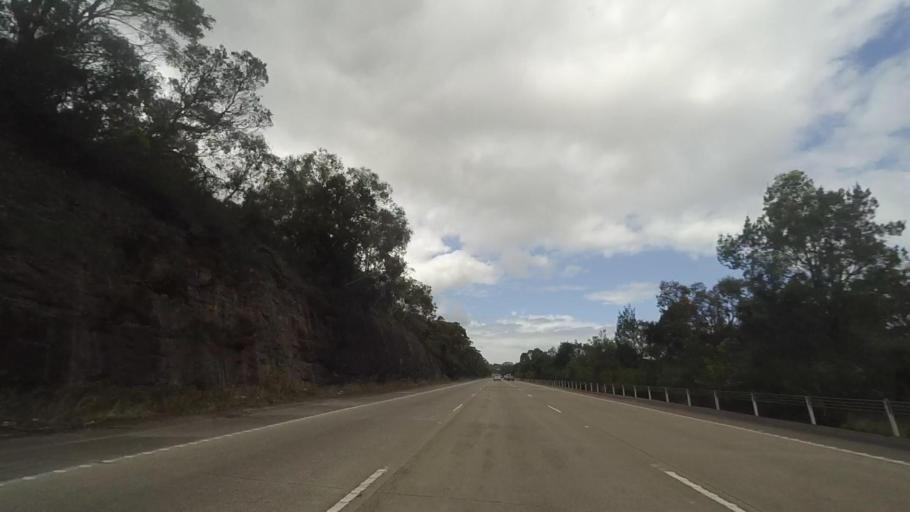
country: AU
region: New South Wales
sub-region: Gosford Shire
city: Point Clare
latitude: -33.4250
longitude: 151.2818
